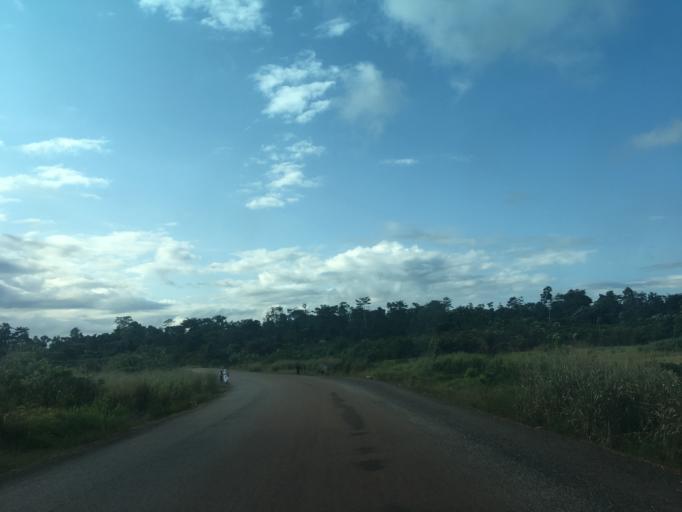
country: GH
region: Western
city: Bibiani
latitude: 6.1153
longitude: -2.3257
